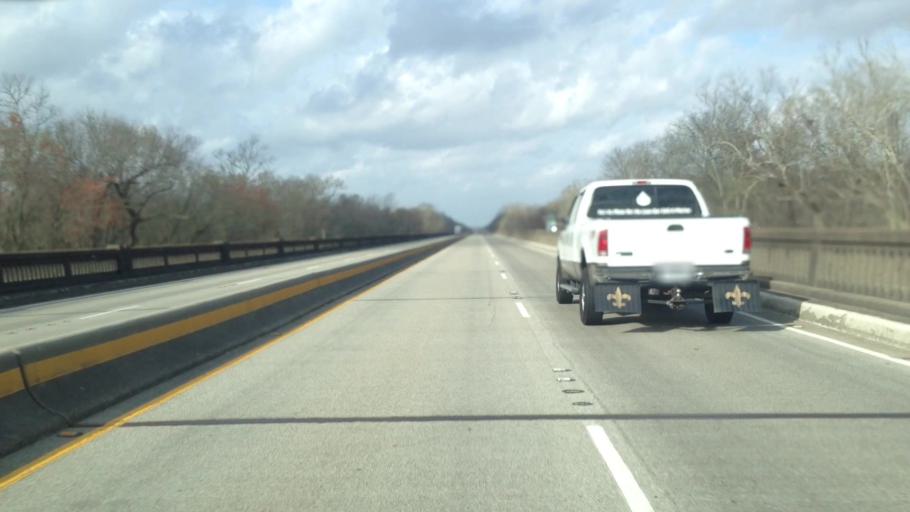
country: US
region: Louisiana
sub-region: Saint Landry Parish
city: Krotz Springs
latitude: 30.5544
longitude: -91.6923
